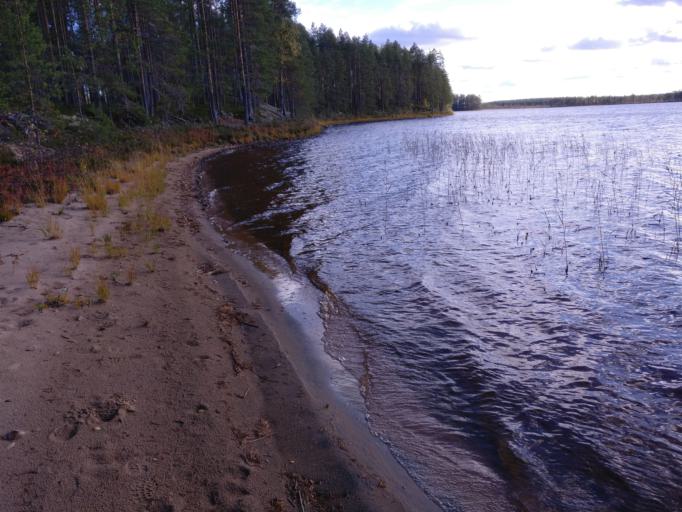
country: FI
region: Northern Savo
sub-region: Koillis-Savo
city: Rautavaara
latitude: 63.6539
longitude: 28.2981
